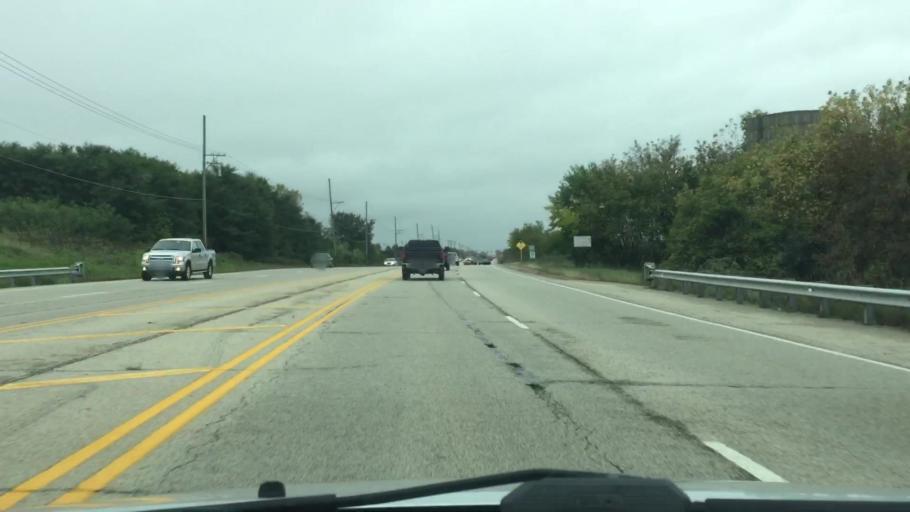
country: US
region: Illinois
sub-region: McHenry County
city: McCullom Lake
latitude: 42.3655
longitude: -88.2674
